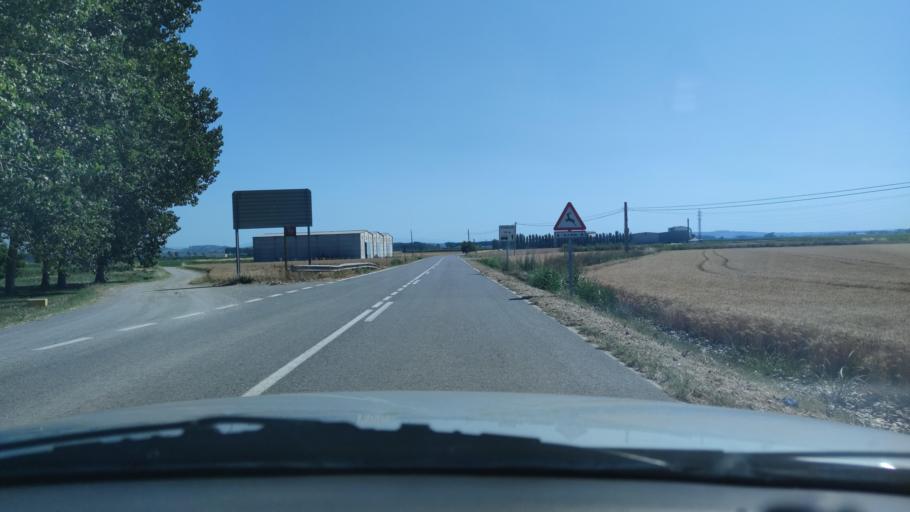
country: ES
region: Catalonia
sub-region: Provincia de Lleida
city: Linyola
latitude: 41.7152
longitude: 0.9088
